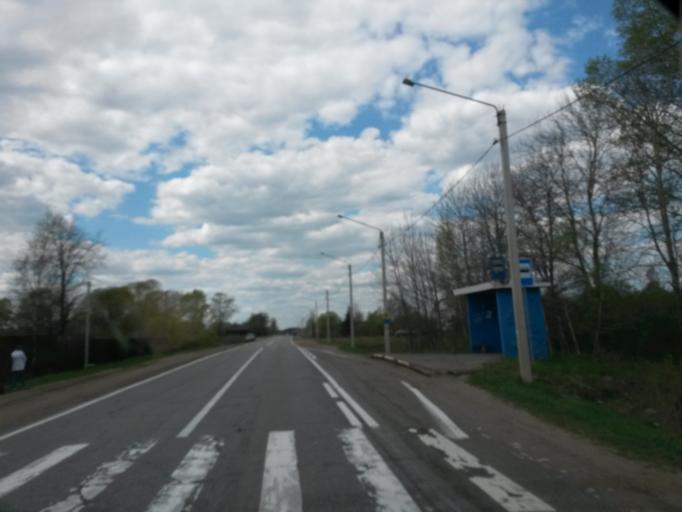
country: RU
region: Jaroslavl
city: Kurba
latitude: 57.6784
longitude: 39.5781
